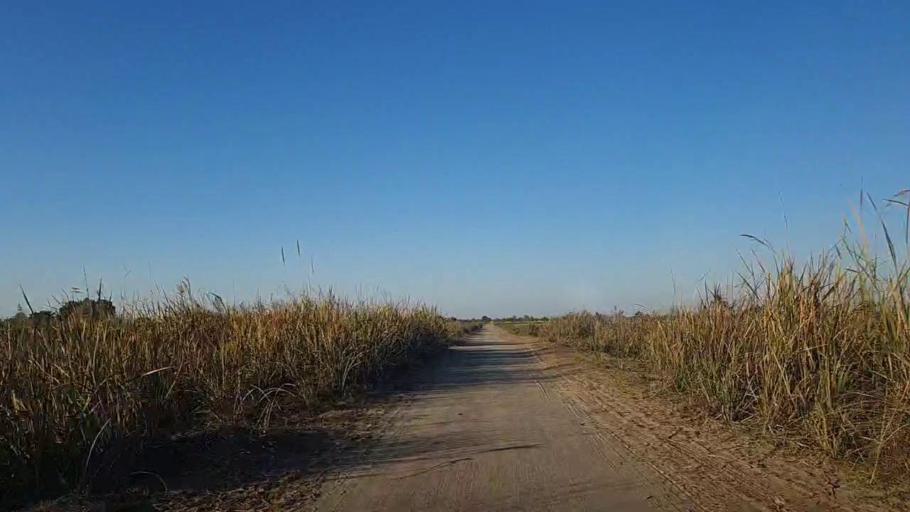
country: PK
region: Sindh
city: Sanghar
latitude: 26.1421
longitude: 68.9265
